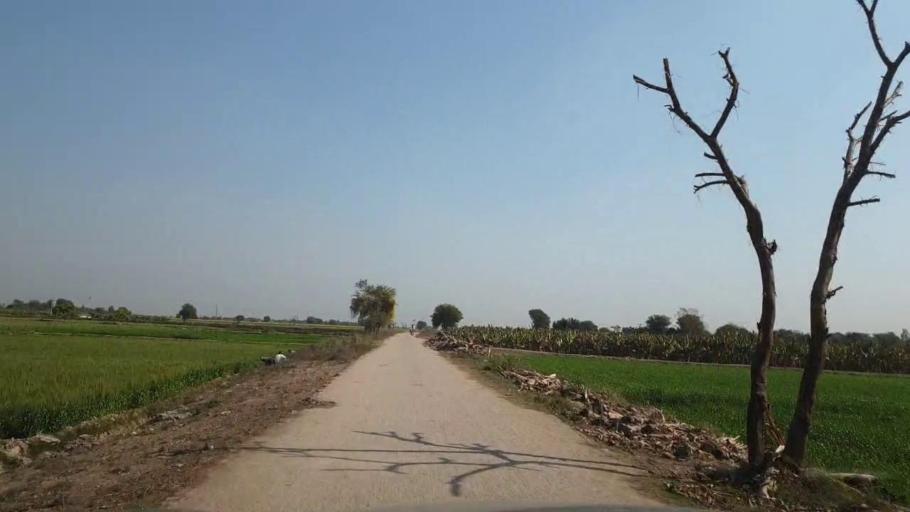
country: PK
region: Sindh
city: Tando Allahyar
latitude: 25.5869
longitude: 68.7501
